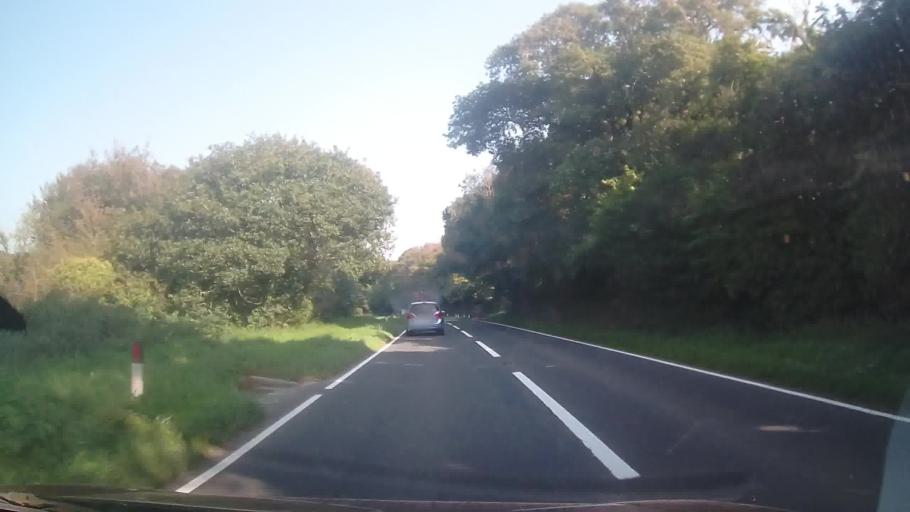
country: GB
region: Wales
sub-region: Pembrokeshire
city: Nevern
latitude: 52.0156
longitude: -4.8153
